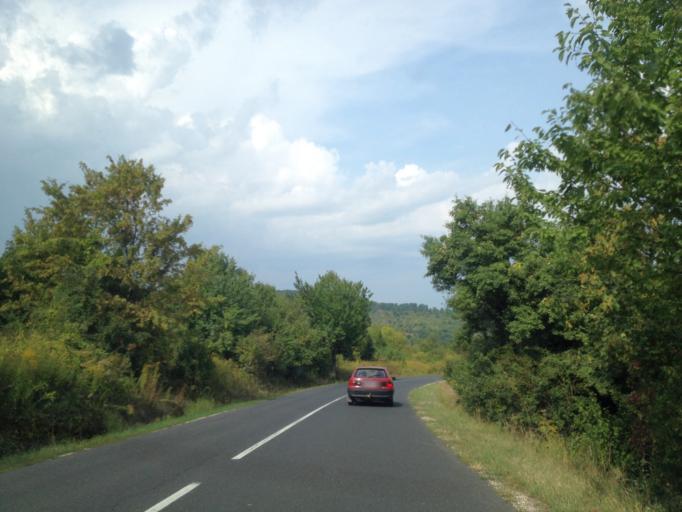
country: HU
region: Komarom-Esztergom
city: Kesztolc
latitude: 47.7279
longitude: 18.8353
